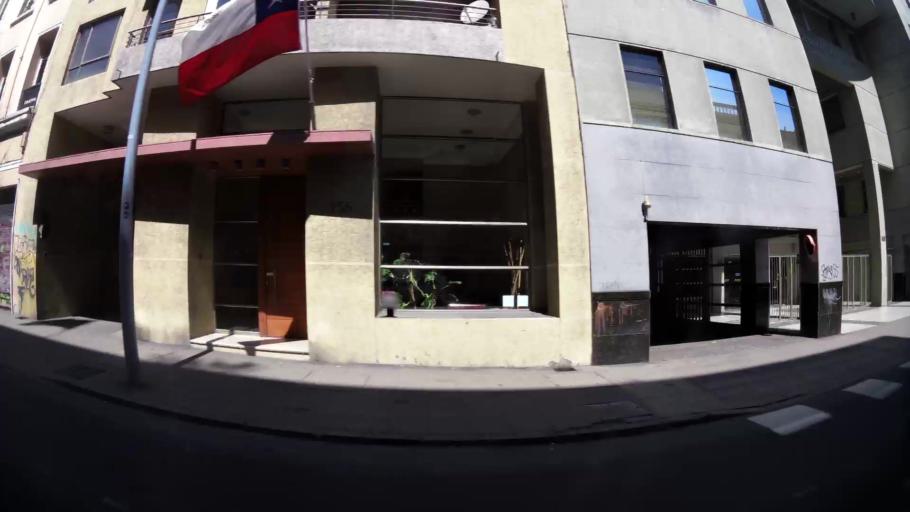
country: CL
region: Santiago Metropolitan
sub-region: Provincia de Santiago
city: Santiago
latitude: -33.4375
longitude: -70.6422
